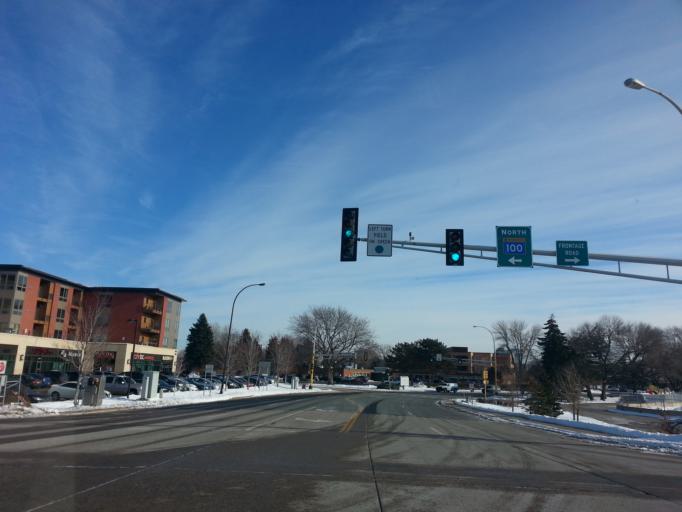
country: US
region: Minnesota
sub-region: Hennepin County
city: Edina
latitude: 44.8641
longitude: -93.3484
